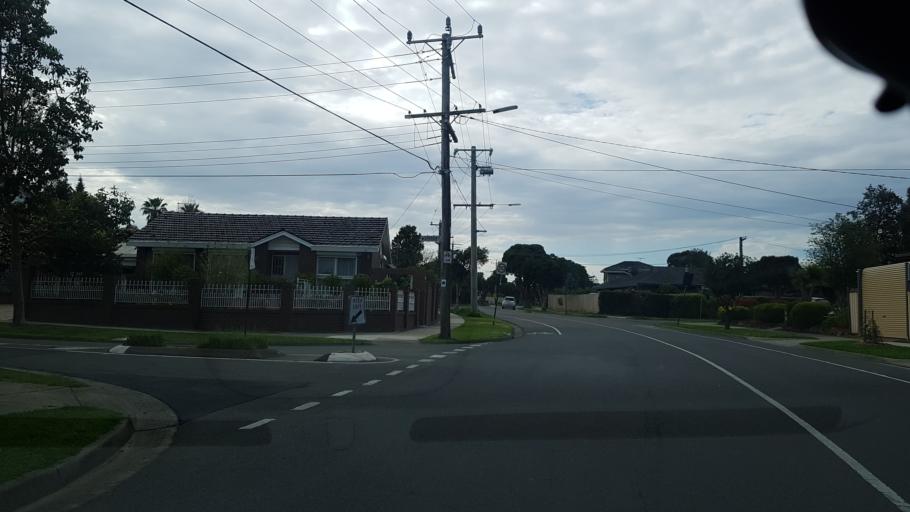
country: AU
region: Victoria
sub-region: Monash
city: Mulgrave
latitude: -37.9118
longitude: 145.1725
